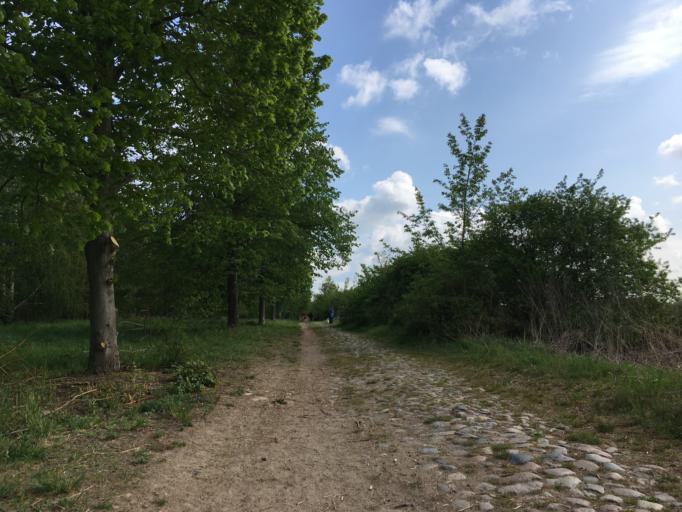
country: DE
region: Berlin
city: Blankenfelde
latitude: 52.6248
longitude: 13.4030
